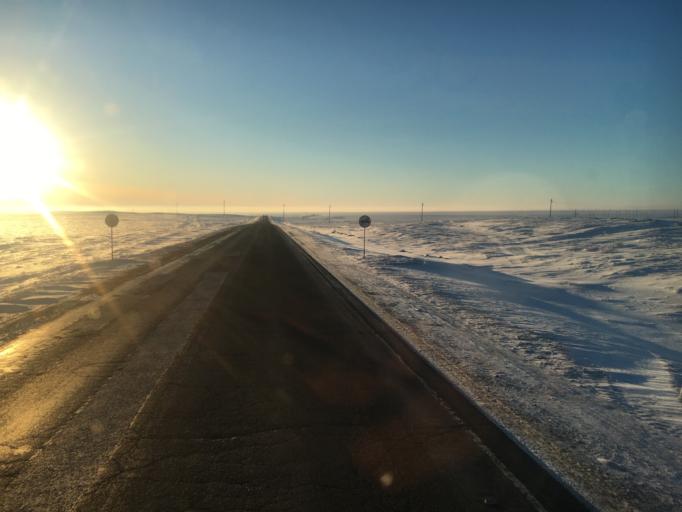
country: KZ
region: Aqtoebe
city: Khromtau
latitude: 50.2567
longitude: 58.3898
